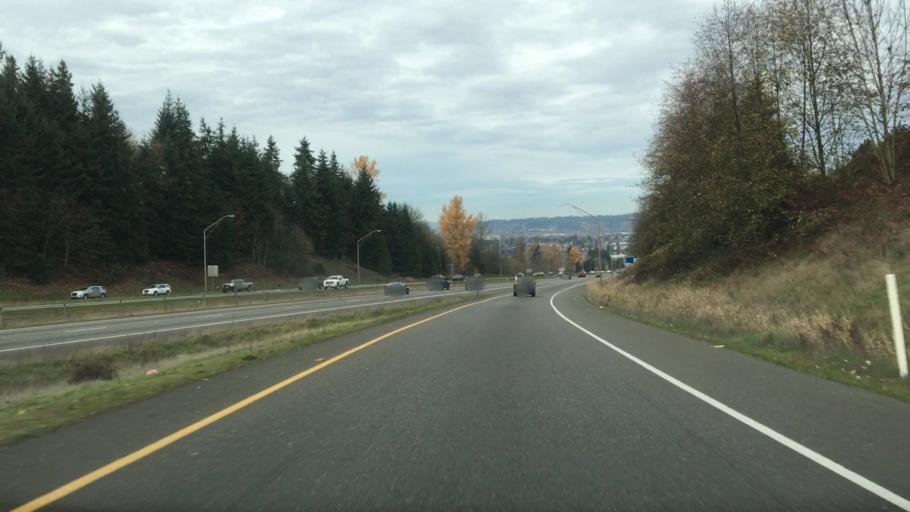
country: US
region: Washington
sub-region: Pierce County
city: Puyallup
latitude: 47.1647
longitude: -122.2962
